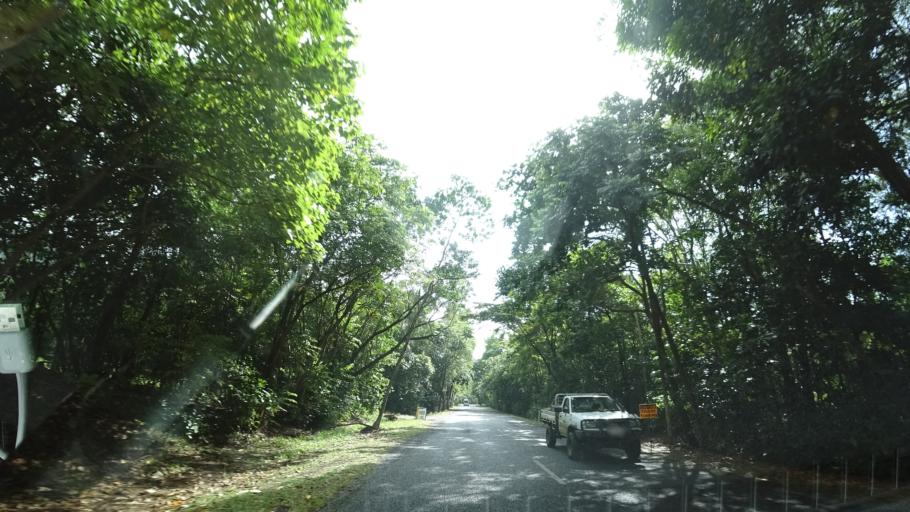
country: AU
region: Queensland
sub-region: Cairns
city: Port Douglas
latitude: -16.0941
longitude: 145.4601
